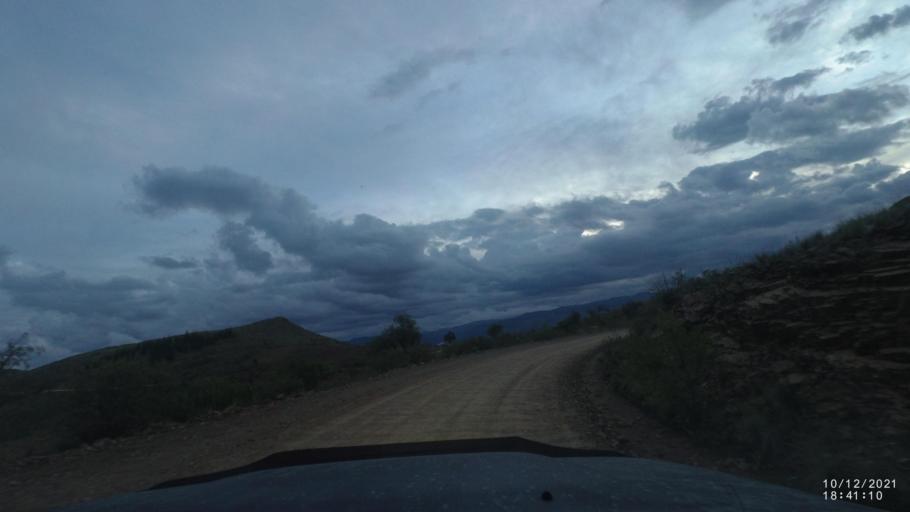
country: BO
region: Cochabamba
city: Tarata
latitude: -17.8613
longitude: -65.9877
